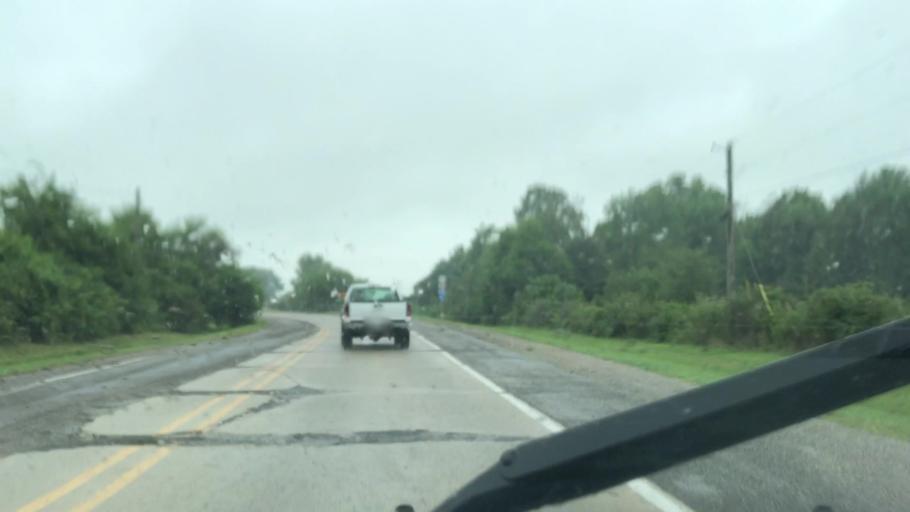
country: US
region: Indiana
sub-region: Boone County
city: Lebanon
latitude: 40.0653
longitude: -86.4931
